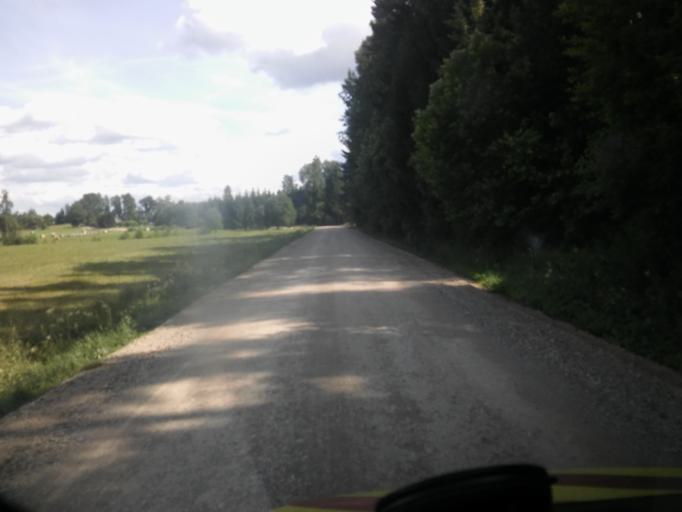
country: EE
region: Viljandimaa
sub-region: Karksi vald
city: Karksi-Nuia
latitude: 58.0594
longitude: 25.5409
